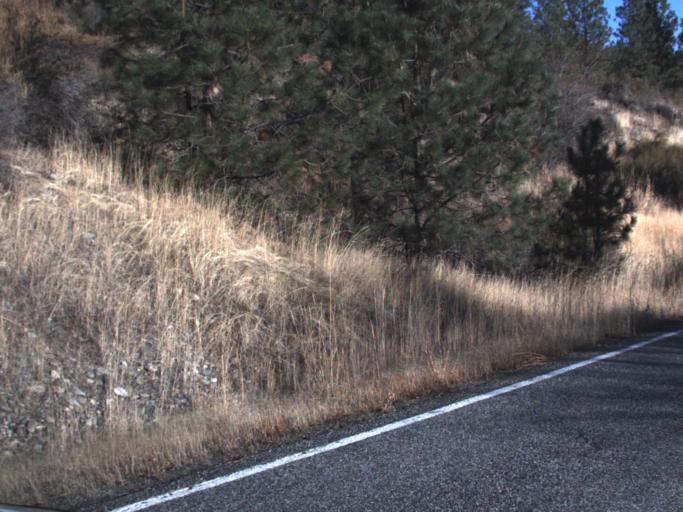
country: US
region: Washington
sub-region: Okanogan County
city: Coulee Dam
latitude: 48.0071
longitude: -118.6869
